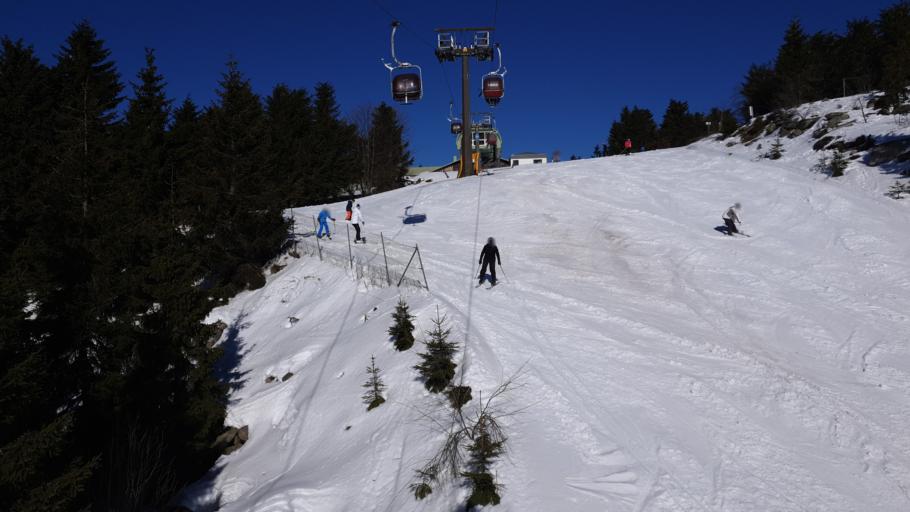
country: DE
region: Bavaria
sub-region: Upper Franconia
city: Bischofsgrun
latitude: 50.0292
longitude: 11.8076
